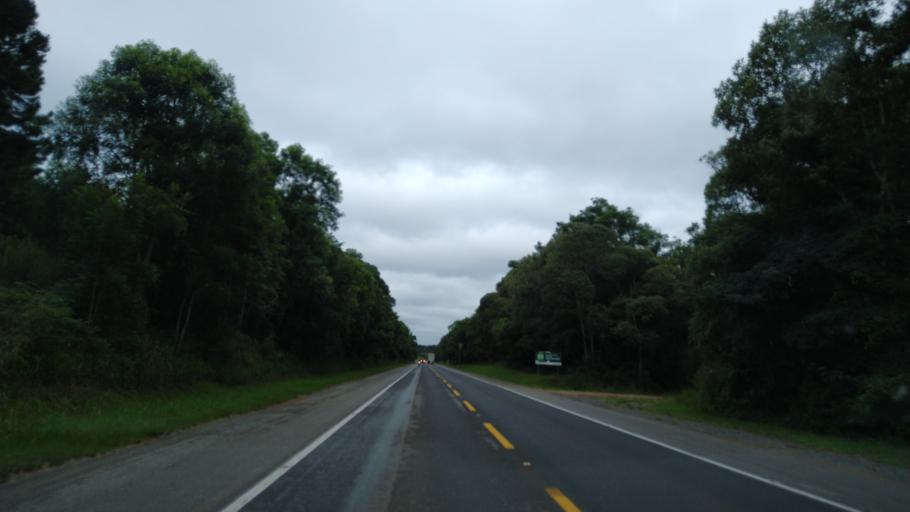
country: BR
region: Santa Catarina
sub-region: Tres Barras
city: Tres Barras
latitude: -26.1713
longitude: -50.0856
